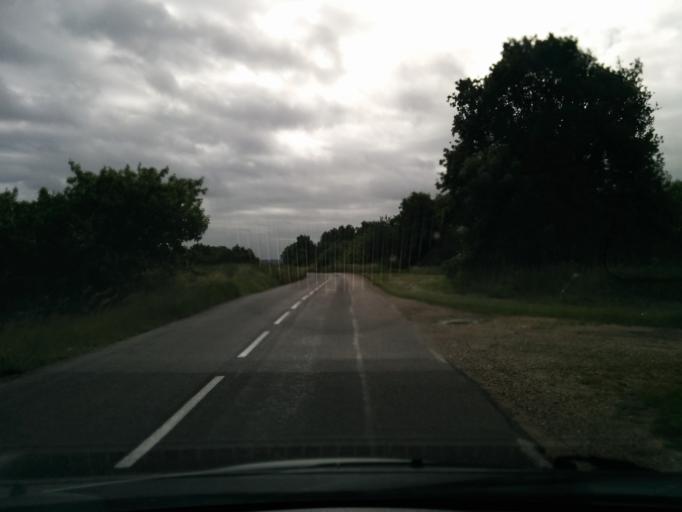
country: FR
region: Ile-de-France
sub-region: Departement des Yvelines
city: Rosny-sur-Seine
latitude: 49.0116
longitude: 1.6448
